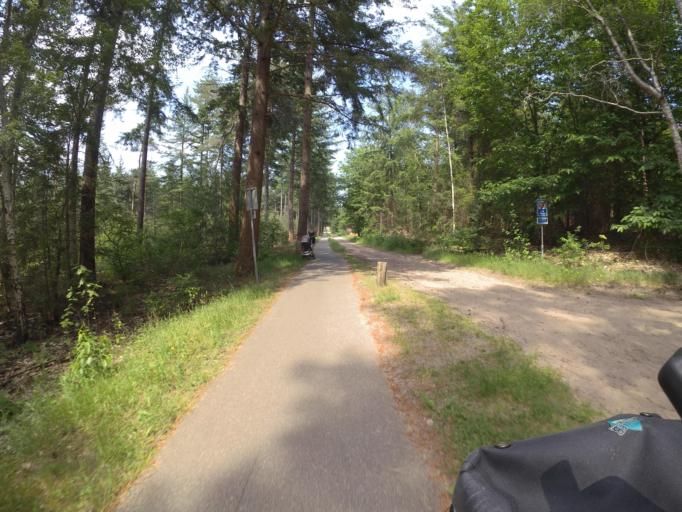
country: NL
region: Overijssel
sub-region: Gemeente Twenterand
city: Den Ham
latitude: 52.3736
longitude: 6.4317
